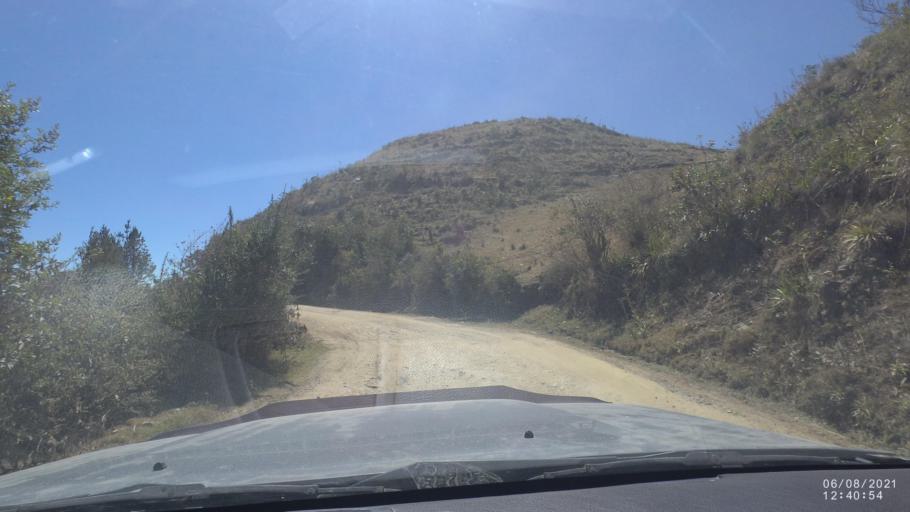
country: BO
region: Cochabamba
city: Colchani
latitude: -16.7841
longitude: -66.6659
